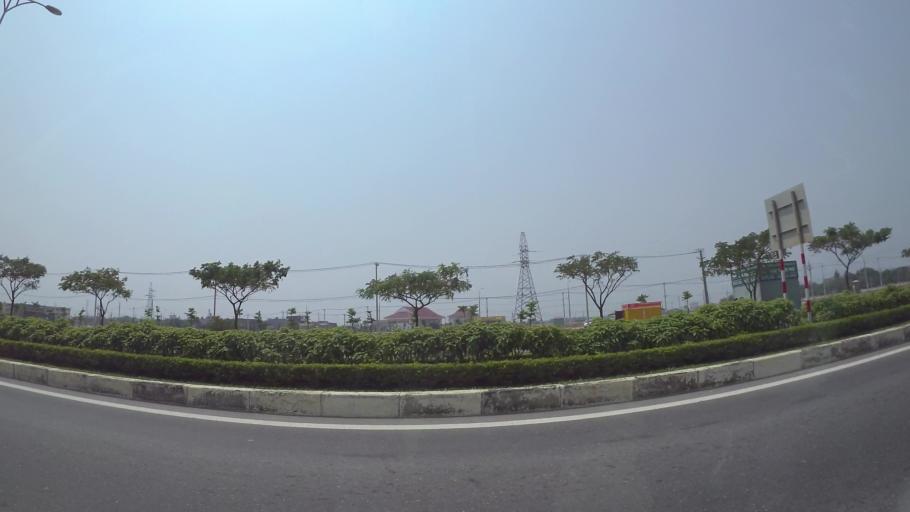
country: VN
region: Da Nang
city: Ngu Hanh Son
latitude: 15.9959
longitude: 108.2350
